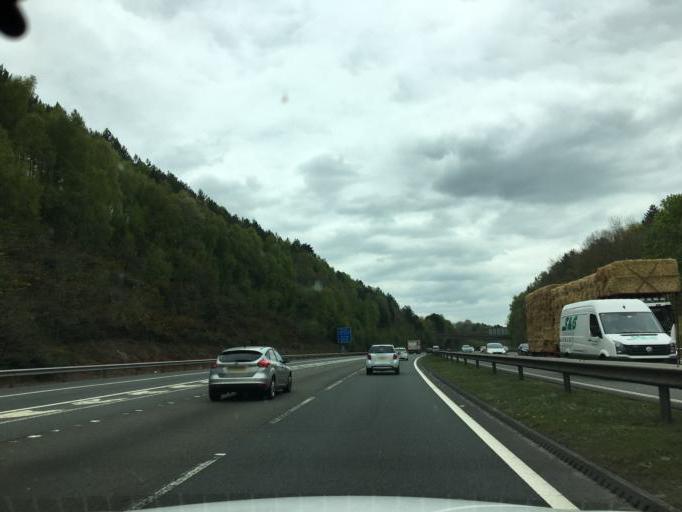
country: GB
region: Wales
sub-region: Cardiff
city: Radyr
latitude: 51.5311
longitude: -3.2311
